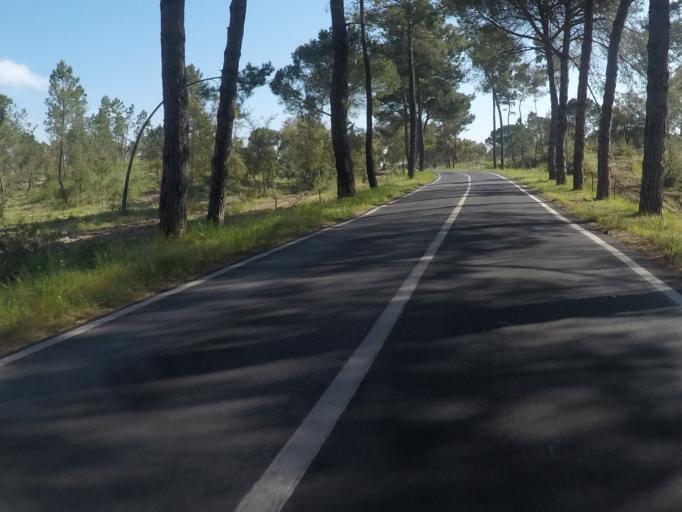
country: PT
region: Setubal
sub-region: Seixal
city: Arrentela
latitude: 38.5417
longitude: -9.1124
